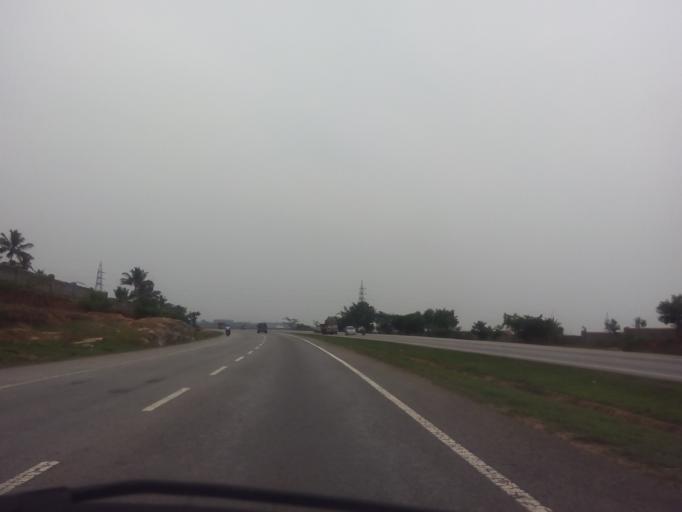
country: IN
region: Karnataka
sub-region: Bangalore Urban
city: Bangalore
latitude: 12.9142
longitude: 77.4676
